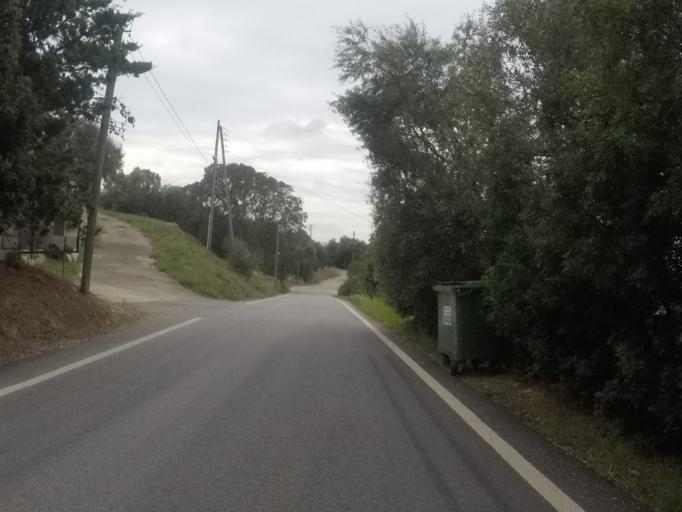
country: FR
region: Corsica
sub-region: Departement de la Corse-du-Sud
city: Pietrosella
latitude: 41.7614
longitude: 8.8132
